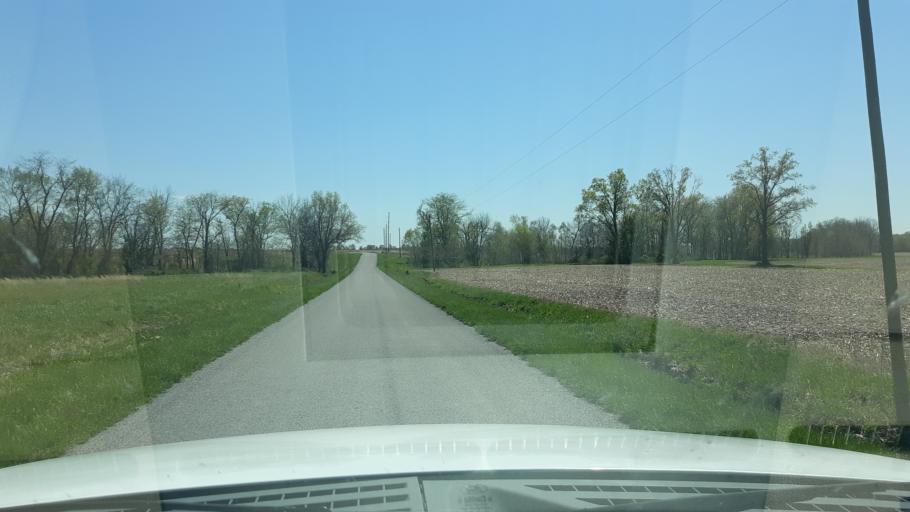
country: US
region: Illinois
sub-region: Saline County
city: Harrisburg
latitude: 37.8879
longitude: -88.6699
